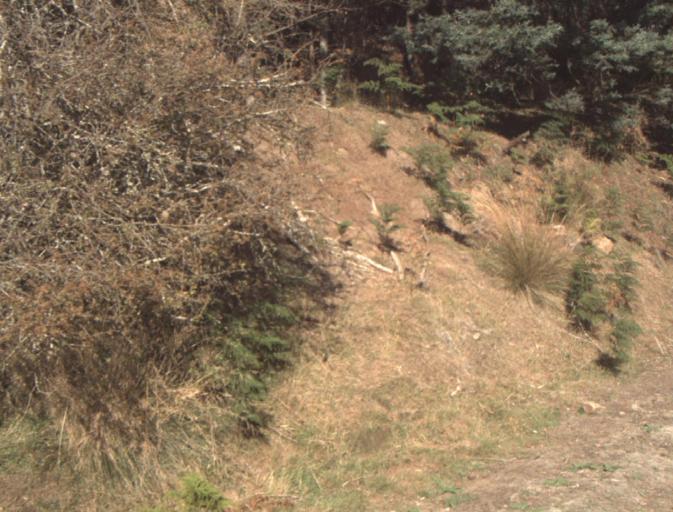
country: AU
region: Tasmania
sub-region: Dorset
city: Scottsdale
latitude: -41.2877
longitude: 147.3593
